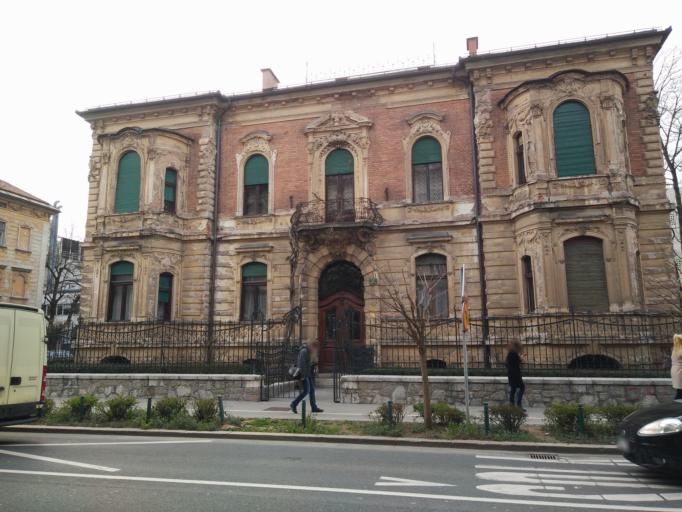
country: SI
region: Ljubljana
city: Ljubljana
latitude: 46.0549
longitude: 14.5108
